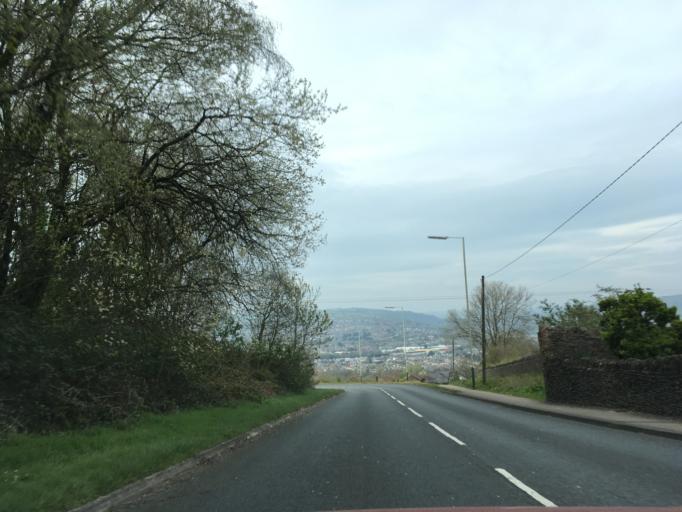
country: GB
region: Wales
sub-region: Caerphilly County Borough
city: Caerphilly
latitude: 51.5629
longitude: -3.2307
